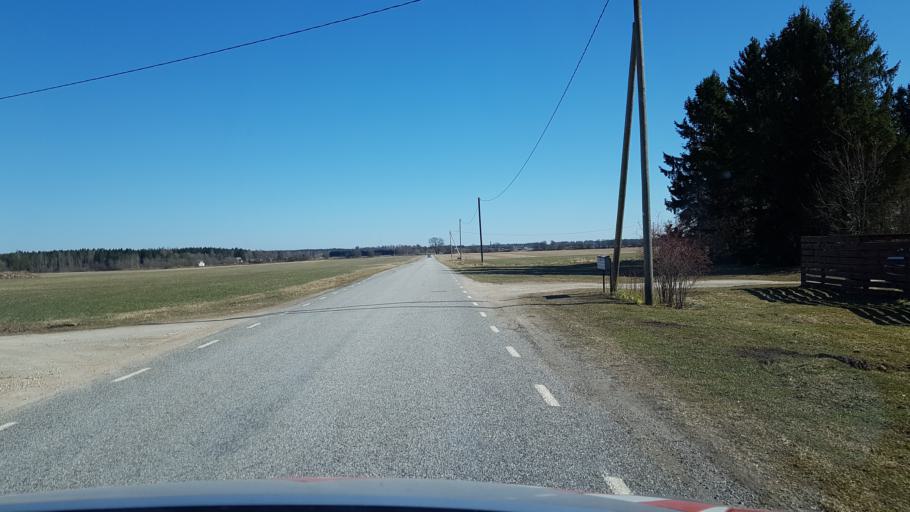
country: EE
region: Laeaene-Virumaa
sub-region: Viru-Nigula vald
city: Kunda
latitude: 59.4067
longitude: 26.5361
